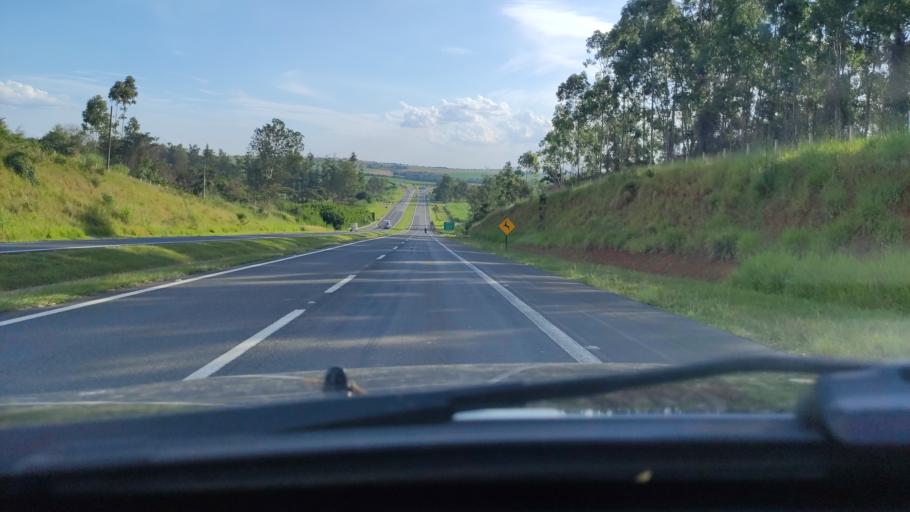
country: BR
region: Sao Paulo
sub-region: Itapira
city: Itapira
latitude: -22.4489
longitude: -46.8873
